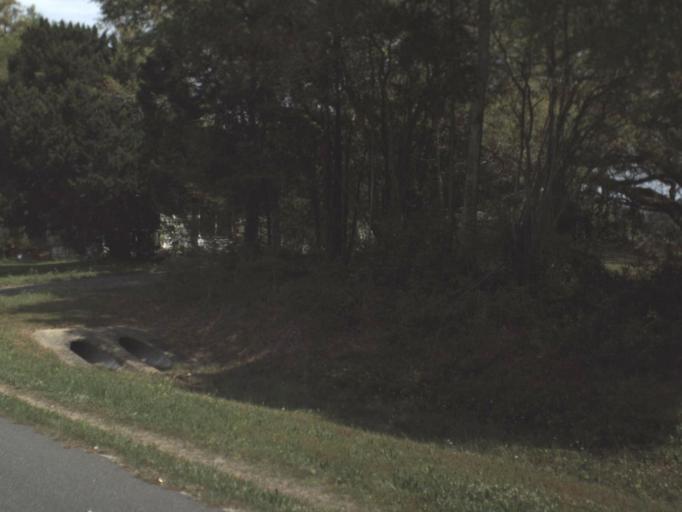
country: US
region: Florida
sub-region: Santa Rosa County
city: Pace
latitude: 30.5981
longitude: -87.1641
